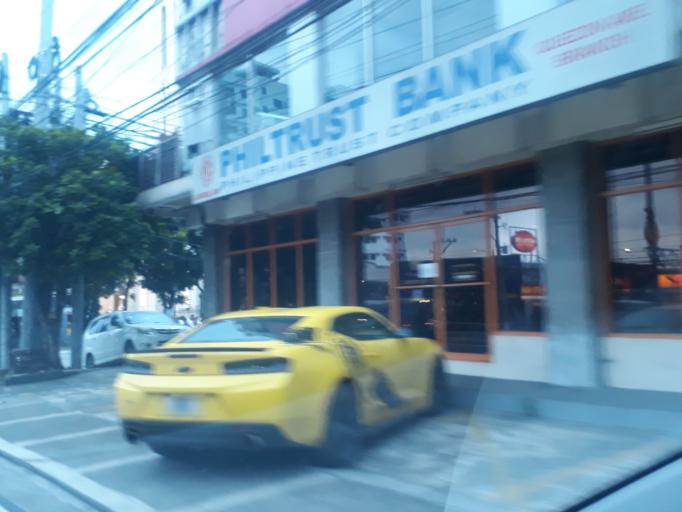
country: PH
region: Calabarzon
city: Del Monte
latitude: 14.6269
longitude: 121.0114
